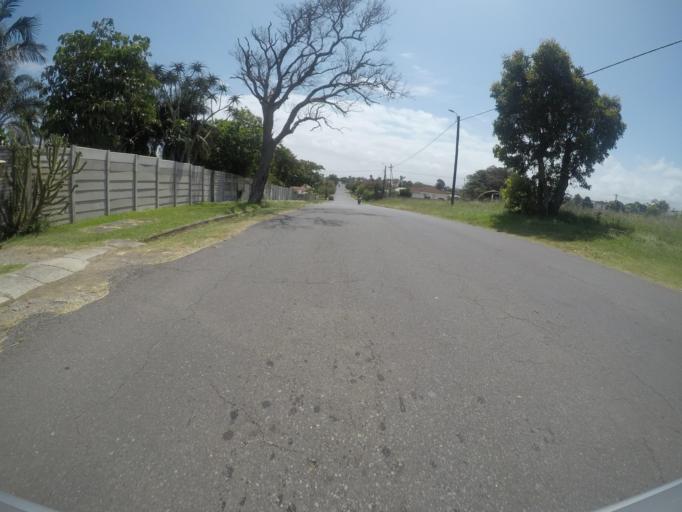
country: ZA
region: Eastern Cape
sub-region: Buffalo City Metropolitan Municipality
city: East London
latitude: -32.9734
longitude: 27.8753
